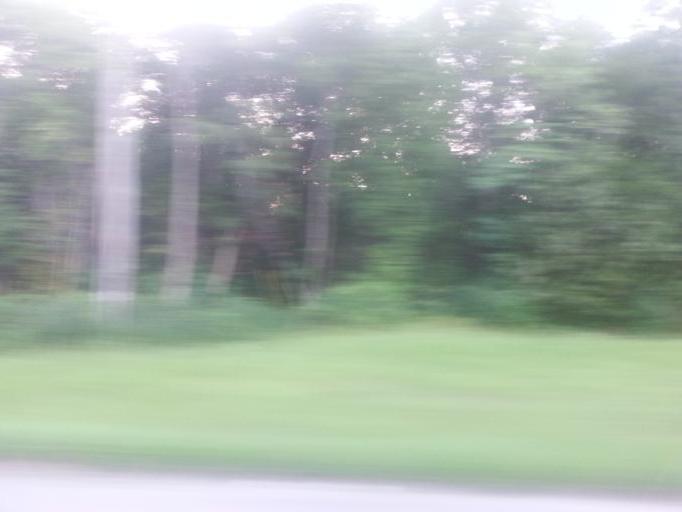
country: US
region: Tennessee
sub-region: Knox County
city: Mascot
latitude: 36.0263
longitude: -83.7355
